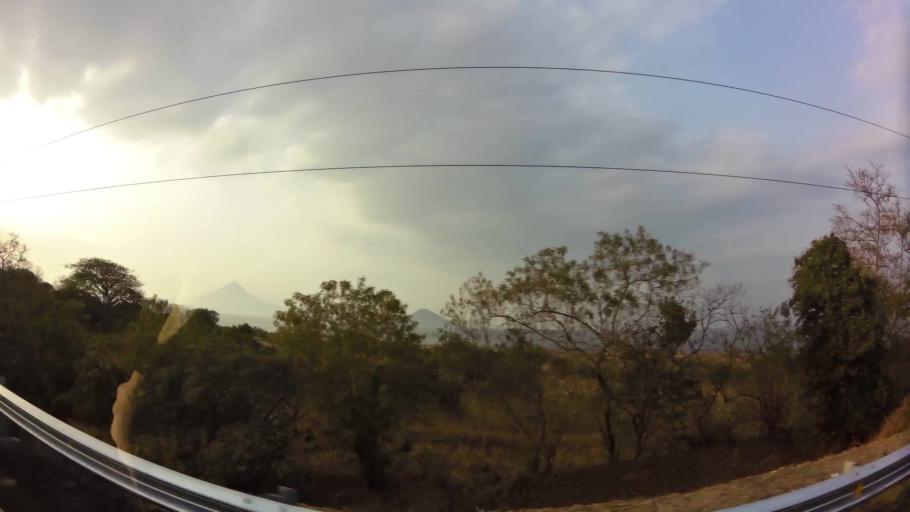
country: NI
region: Leon
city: Nagarote
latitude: 12.2695
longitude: -86.4791
